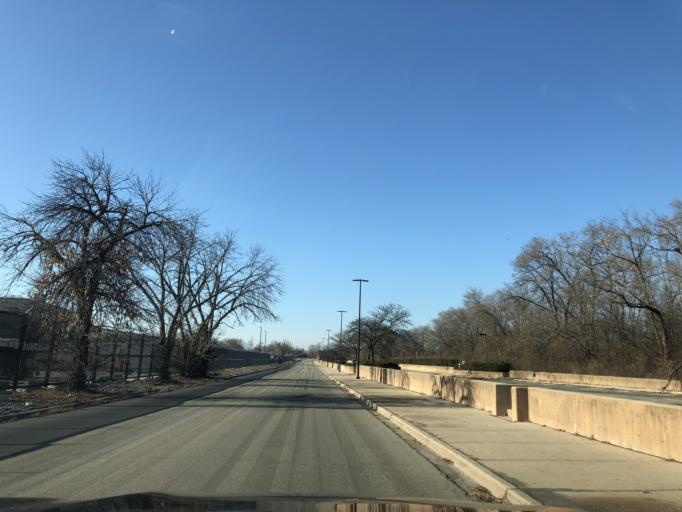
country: US
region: Illinois
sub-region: Cook County
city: Forest Park
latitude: 41.8752
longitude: -87.8281
